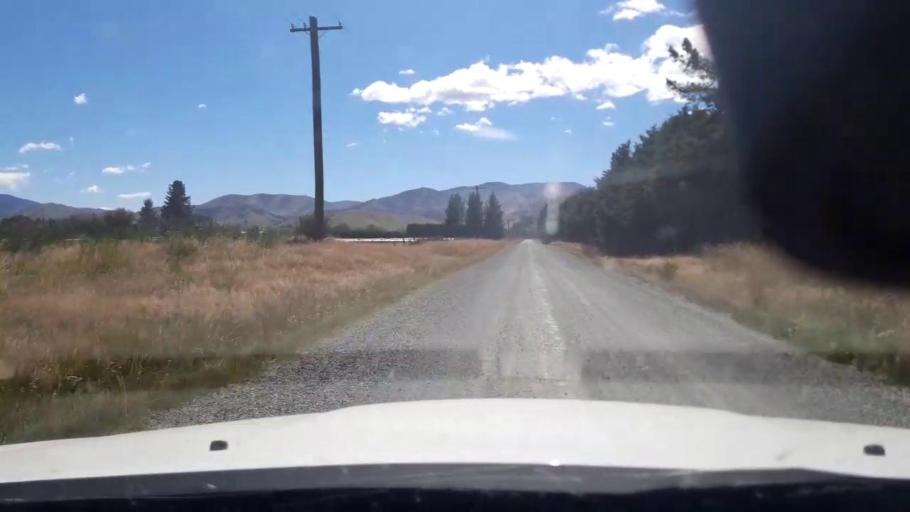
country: NZ
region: Canterbury
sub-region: Timaru District
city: Pleasant Point
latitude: -44.0021
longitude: 170.8380
